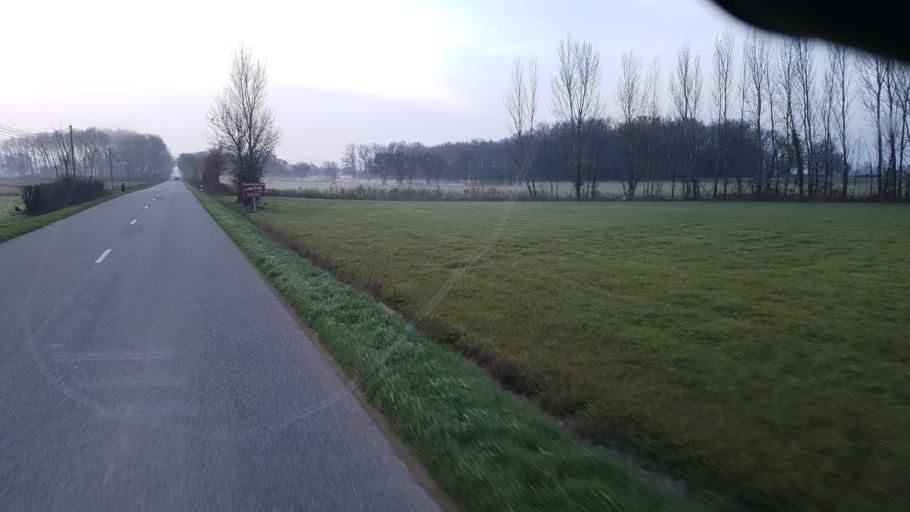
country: FR
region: Midi-Pyrenees
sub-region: Departement du Tarn-et-Garonne
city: Montricoux
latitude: 44.0963
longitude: 1.6040
